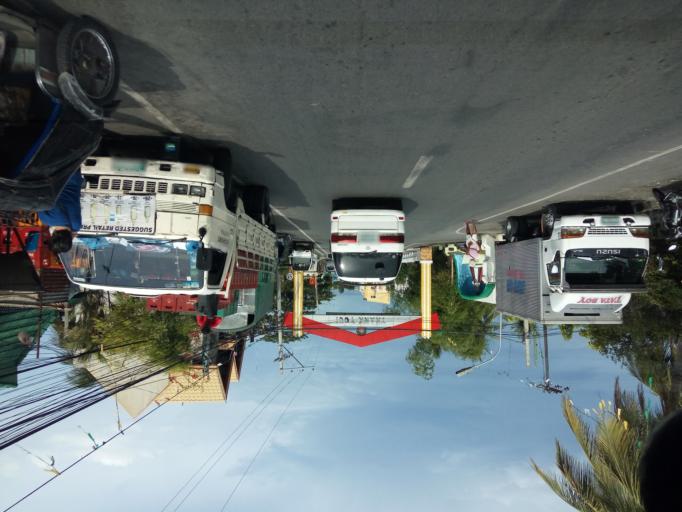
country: PH
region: Central Luzon
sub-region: Province of Nueva Ecija
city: Sibul
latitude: 15.7951
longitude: 120.9873
